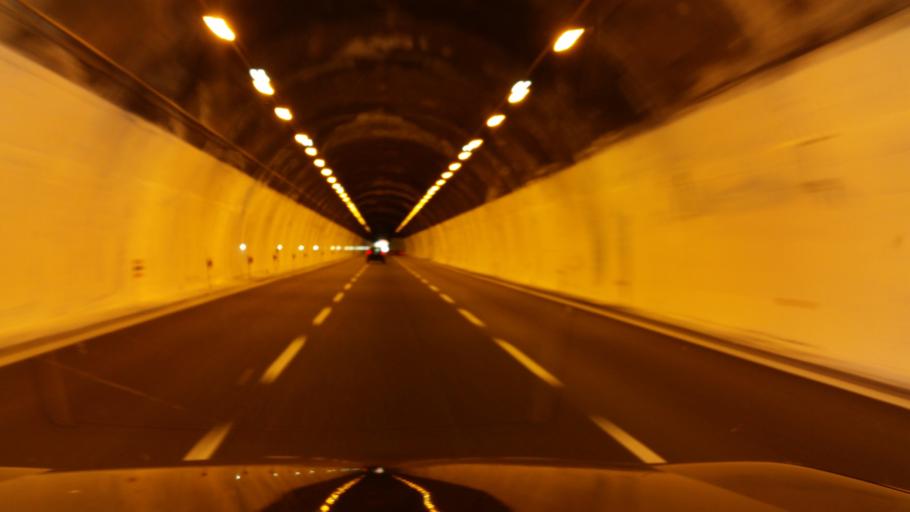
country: IT
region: Liguria
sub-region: Provincia di Genova
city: Cogoleto
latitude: 44.3909
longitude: 8.6325
